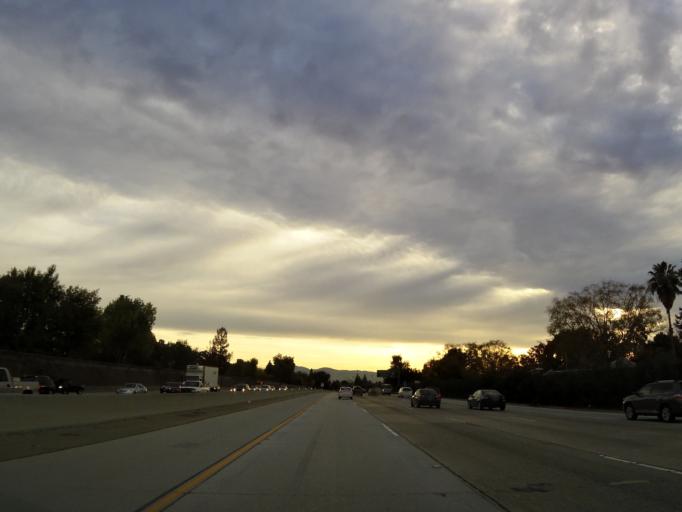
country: US
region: California
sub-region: Santa Clara County
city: Campbell
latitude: 37.3180
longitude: -121.9821
